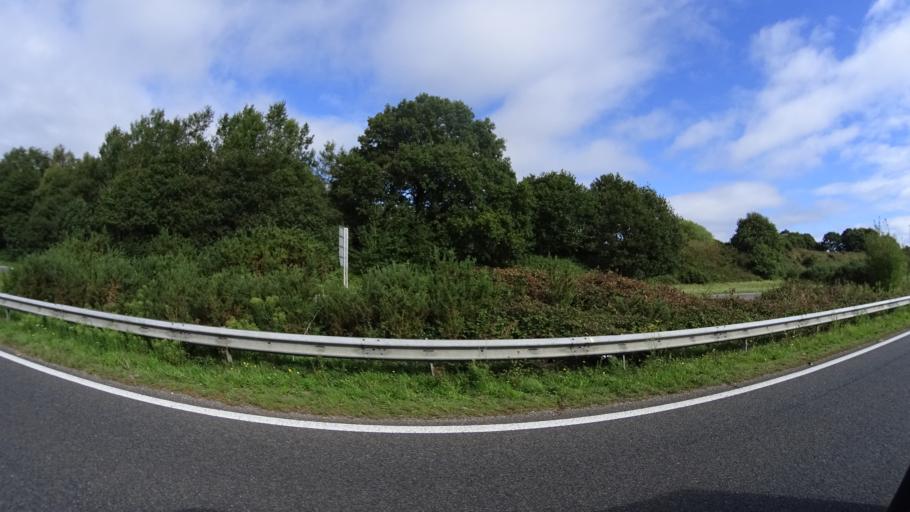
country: GB
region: England
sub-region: Dorset
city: Lytchett Matravers
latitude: 50.7429
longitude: -2.0370
